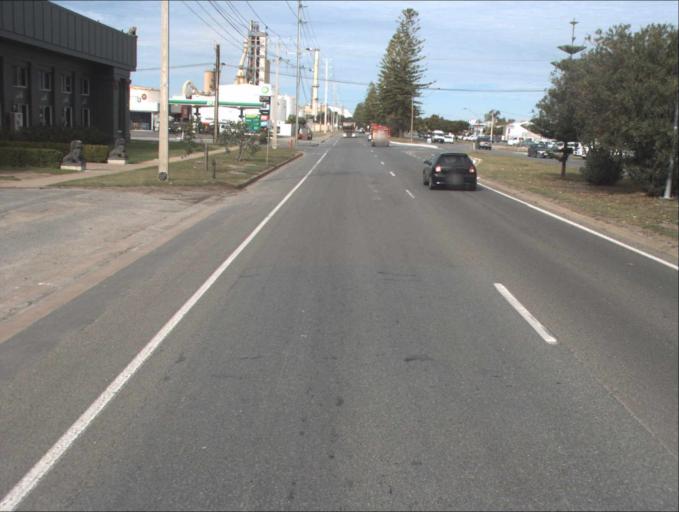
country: AU
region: South Australia
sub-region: Port Adelaide Enfield
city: Birkenhead
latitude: -34.8244
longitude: 138.5000
